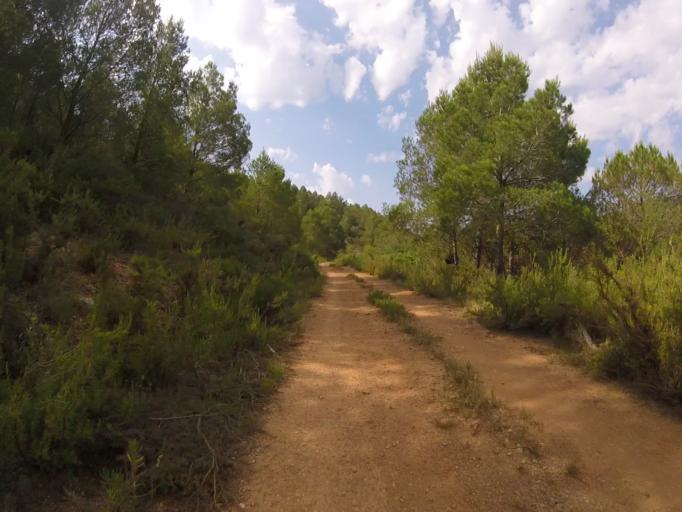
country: ES
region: Valencia
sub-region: Provincia de Castello
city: Alcala de Xivert
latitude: 40.3515
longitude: 0.1997
